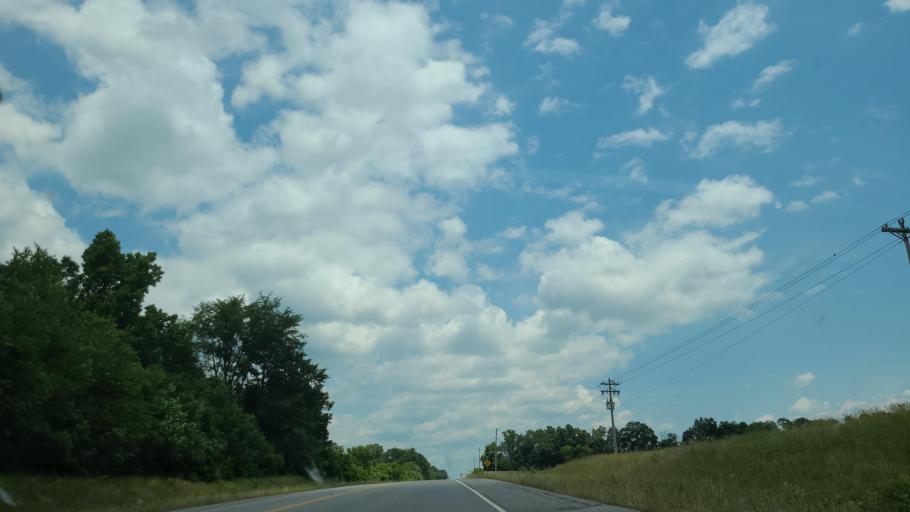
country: US
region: Tennessee
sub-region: Bledsoe County
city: Pikeville
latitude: 35.6203
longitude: -85.1839
